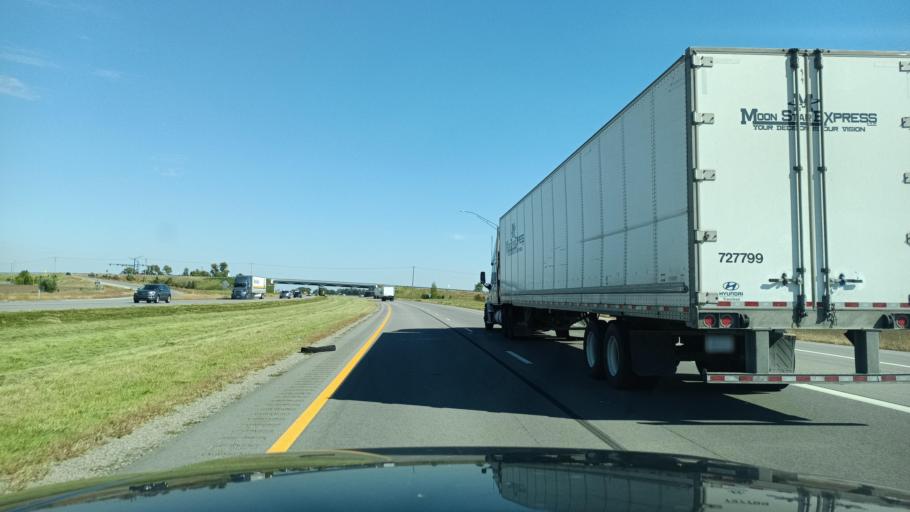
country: US
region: Ohio
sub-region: Defiance County
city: Defiance
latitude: 41.3096
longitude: -84.3280
